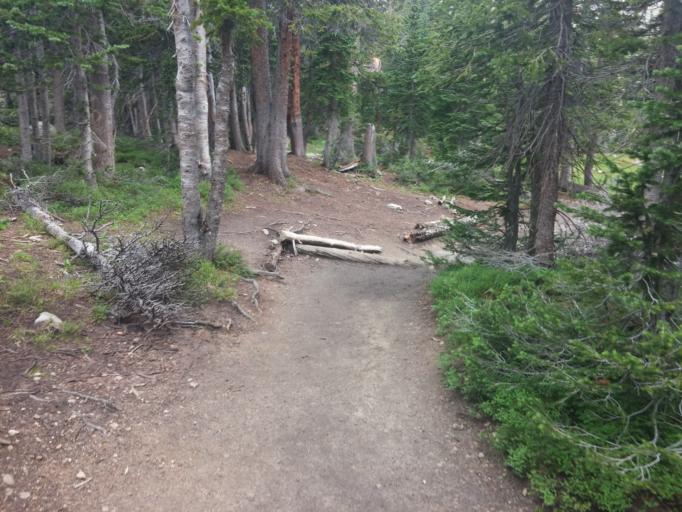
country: US
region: Colorado
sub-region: Boulder County
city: Nederland
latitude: 40.0865
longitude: -105.5943
